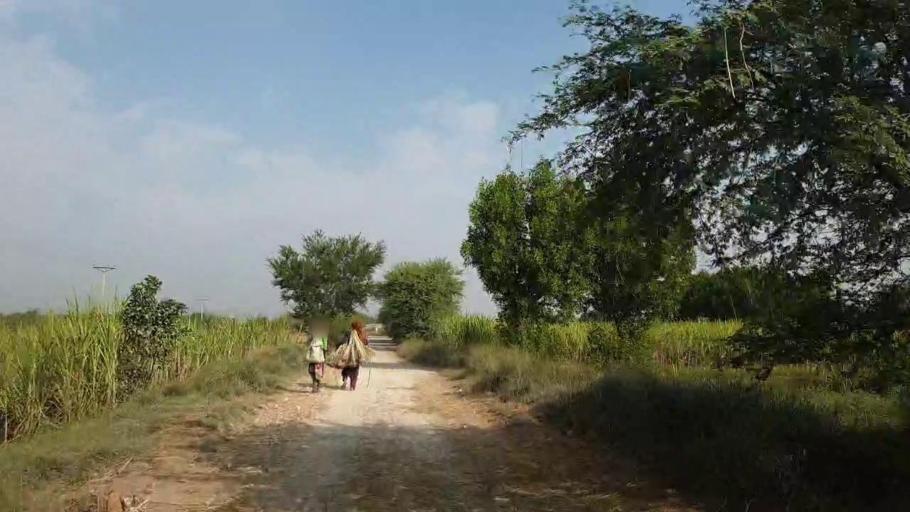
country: PK
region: Sindh
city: Tando Muhammad Khan
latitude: 25.0490
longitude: 68.4359
